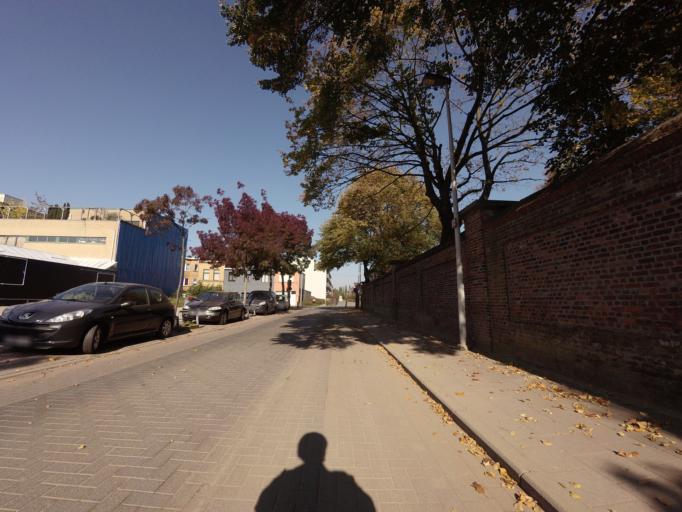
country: BE
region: Flanders
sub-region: Provincie Antwerpen
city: Borsbeek
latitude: 51.2048
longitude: 4.4754
